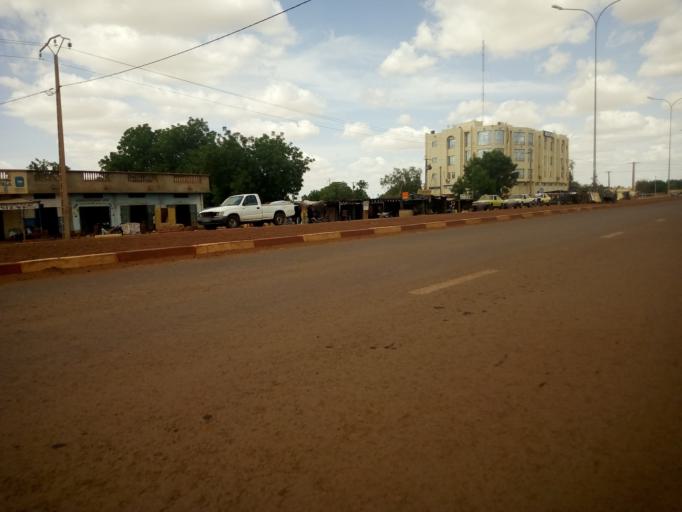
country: ML
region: Segou
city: Segou
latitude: 13.4325
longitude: -6.2277
